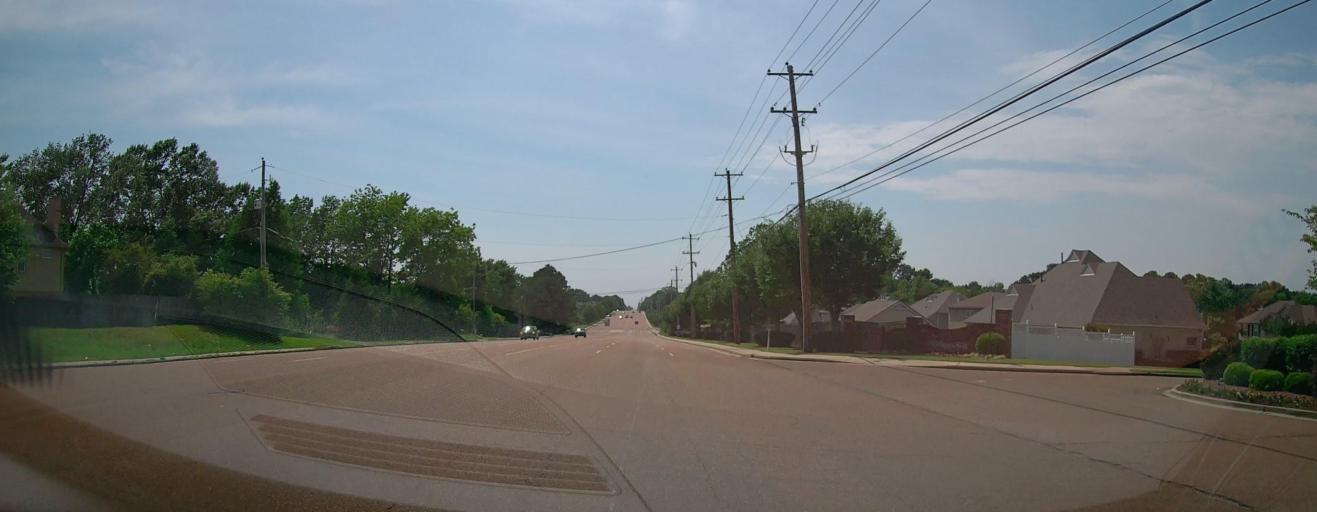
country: US
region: Mississippi
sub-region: De Soto County
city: Olive Branch
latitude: 35.0205
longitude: -89.8051
